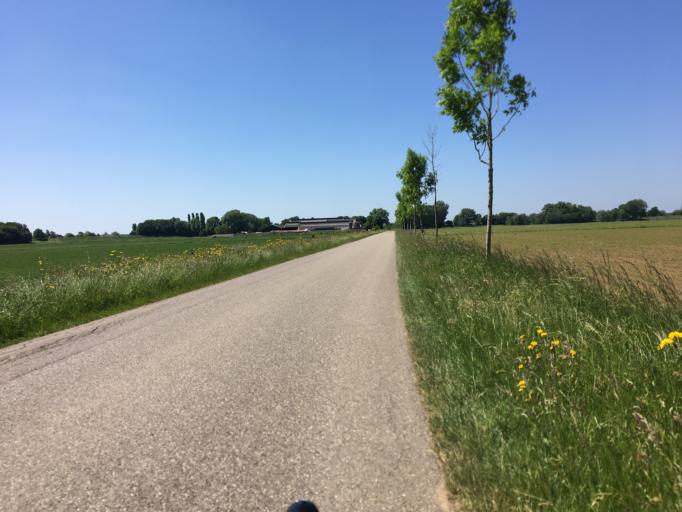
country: NL
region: Gelderland
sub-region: Gemeente Zaltbommel
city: Nederhemert-Noord
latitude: 51.7359
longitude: 5.1972
